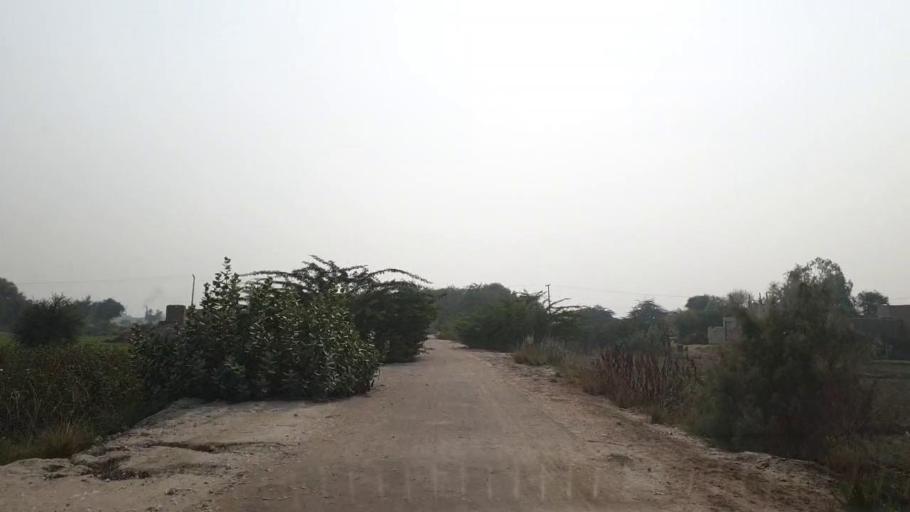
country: PK
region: Sindh
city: Bhan
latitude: 26.5409
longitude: 67.7167
